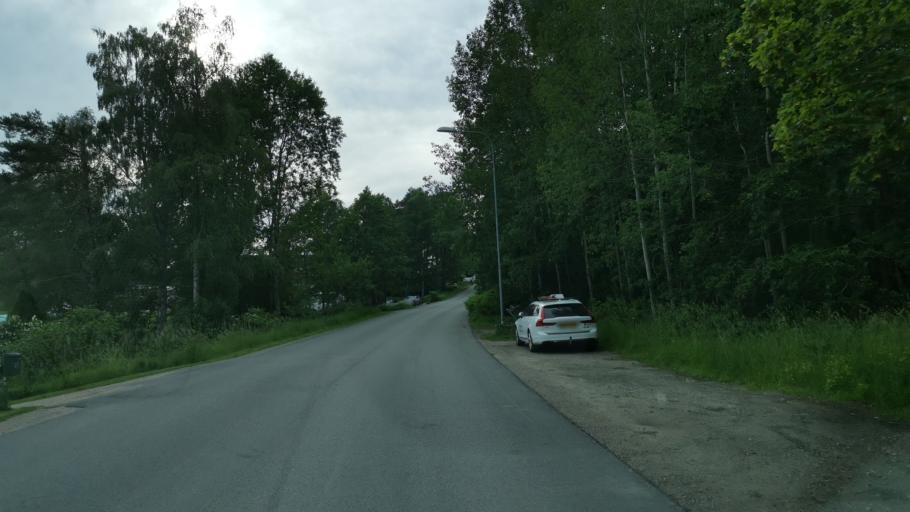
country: SE
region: Vaestra Goetaland
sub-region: Vanersborgs Kommun
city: Vargon
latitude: 58.3597
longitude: 12.3609
